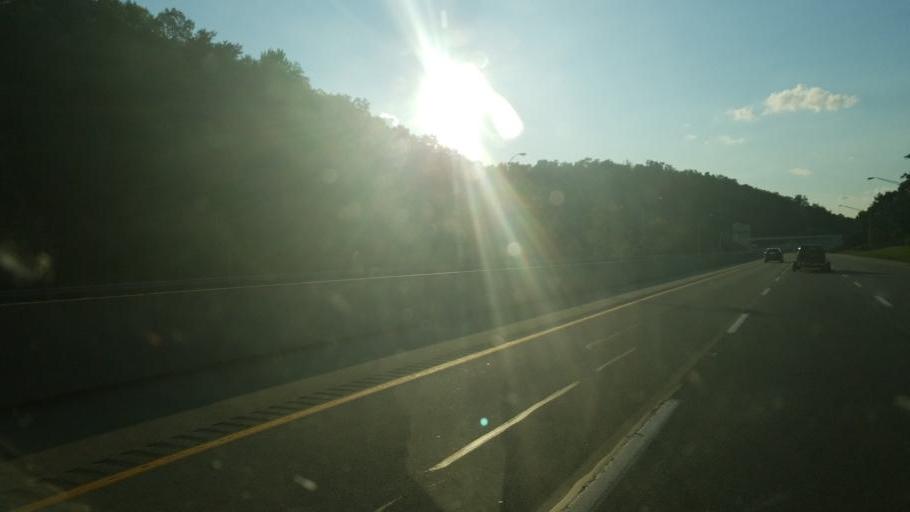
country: US
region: Pennsylvania
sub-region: Beaver County
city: Big Beaver
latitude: 40.8396
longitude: -80.3827
